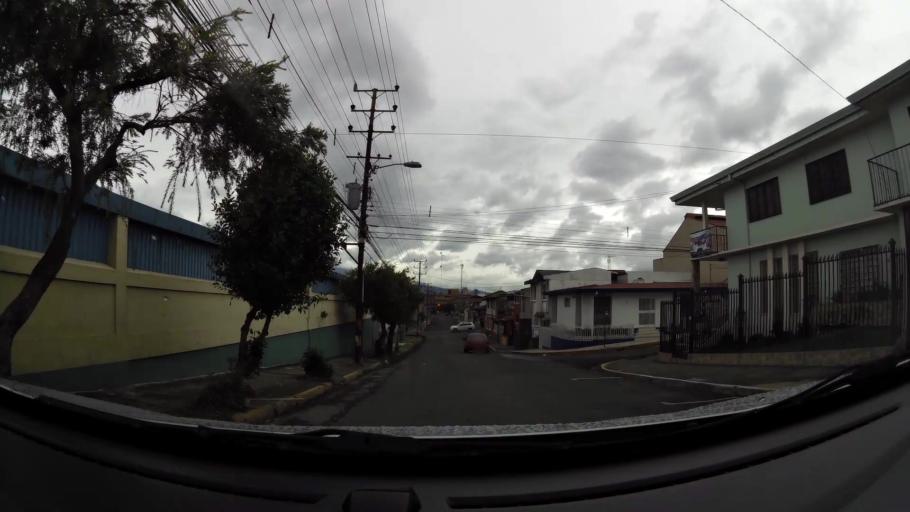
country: CR
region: San Jose
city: San Jose
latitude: 9.9323
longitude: -84.0909
